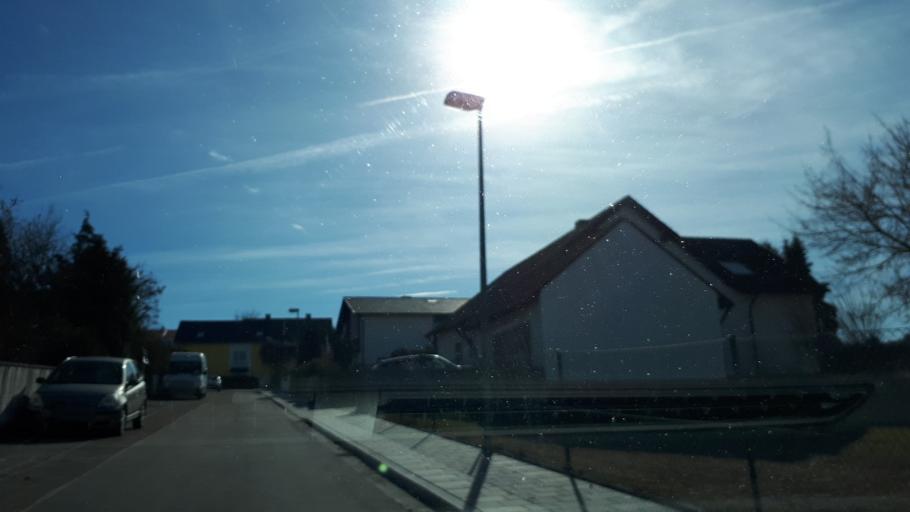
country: DE
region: Bavaria
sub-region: Upper Palatinate
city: Pentling
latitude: 48.9809
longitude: 12.0547
